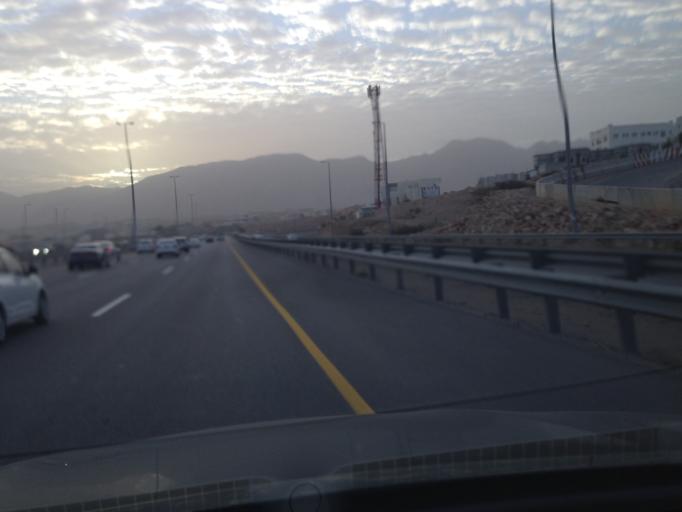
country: OM
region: Muhafazat Masqat
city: Bawshar
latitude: 23.5653
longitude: 58.3823
